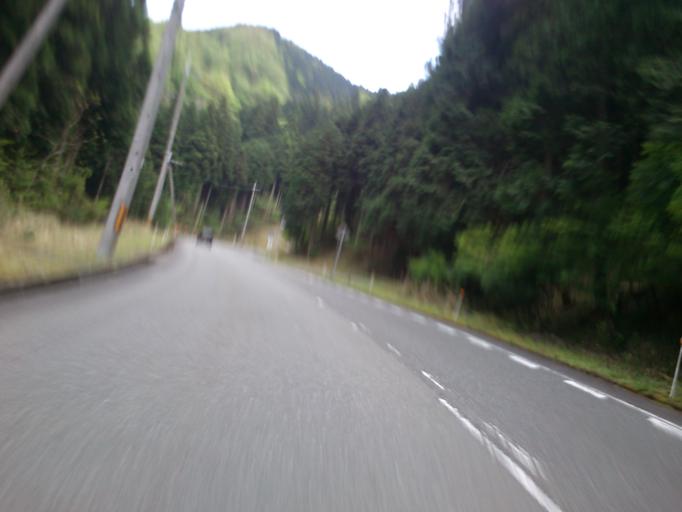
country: JP
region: Kyoto
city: Fukuchiyama
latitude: 35.3020
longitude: 135.0094
